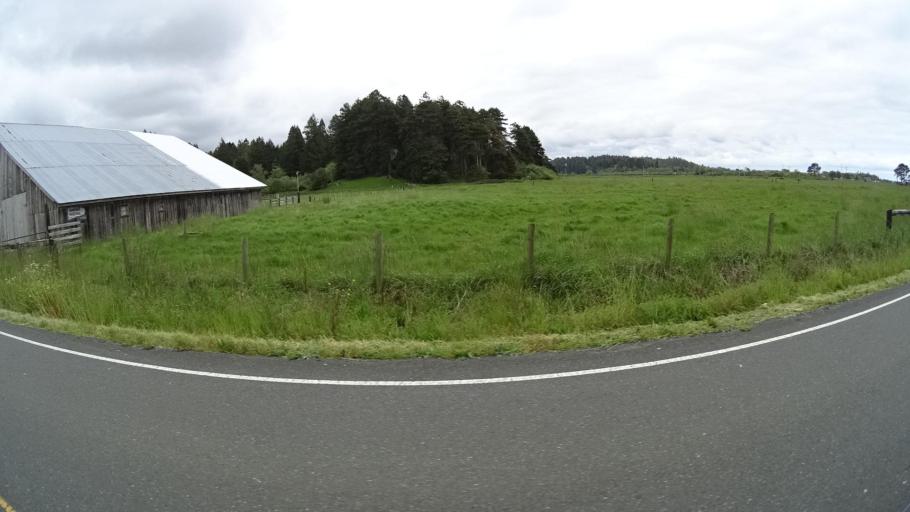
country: US
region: California
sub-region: Humboldt County
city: Bayside
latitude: 40.8350
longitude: -124.0750
